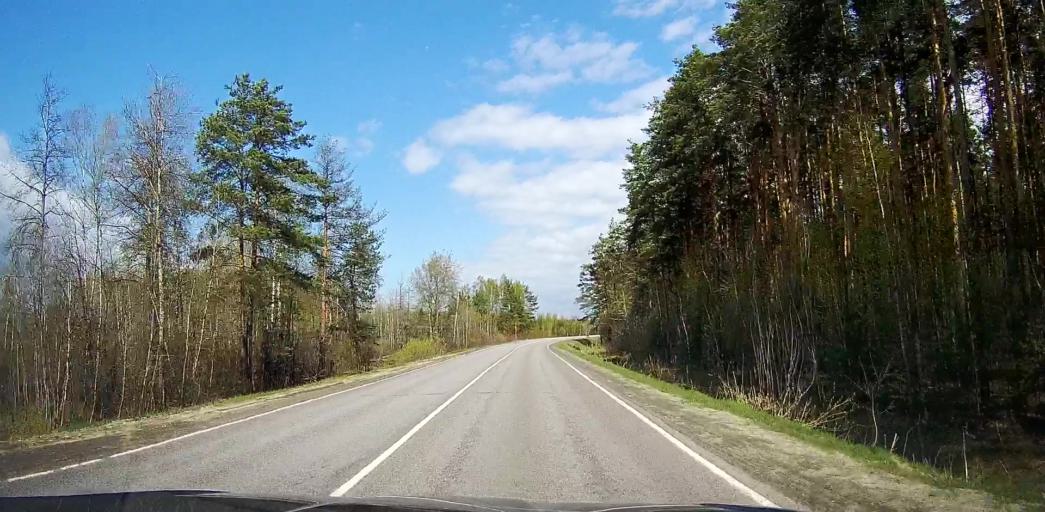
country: RU
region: Moskovskaya
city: Davydovo
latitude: 55.5509
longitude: 38.8183
